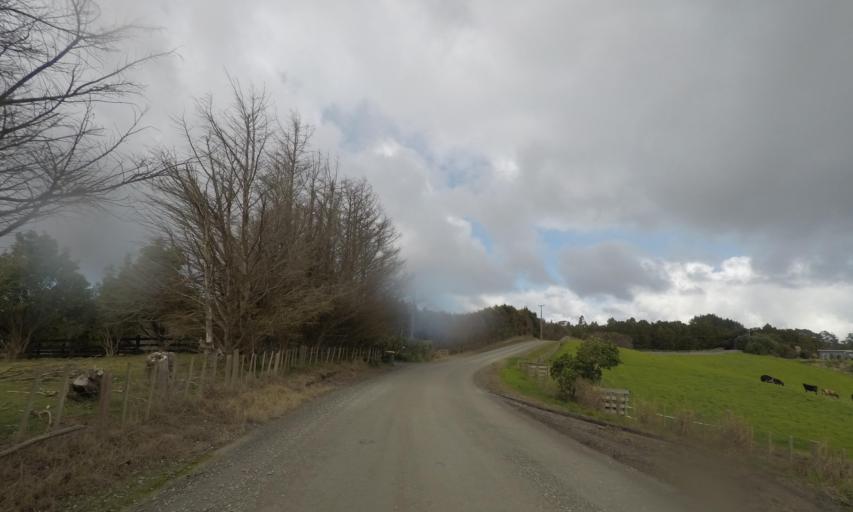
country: NZ
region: Auckland
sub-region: Auckland
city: Wellsford
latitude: -36.1673
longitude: 174.6028
